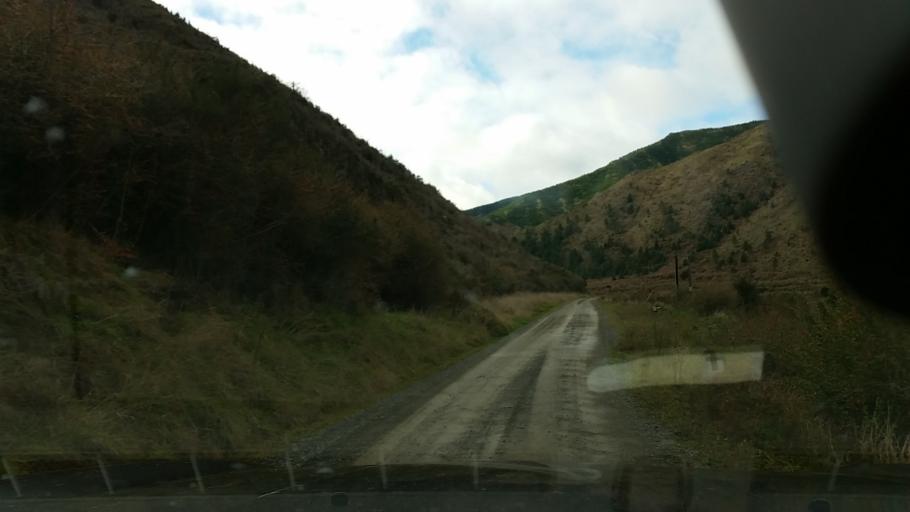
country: NZ
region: Tasman
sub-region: Tasman District
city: Richmond
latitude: -41.7131
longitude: 173.4795
